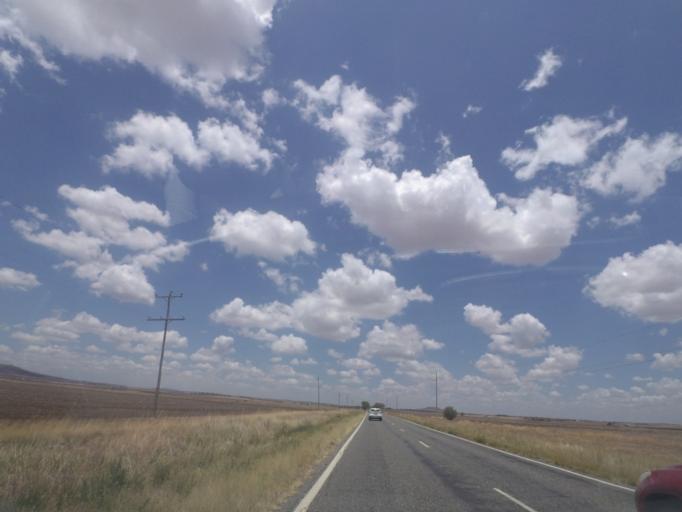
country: AU
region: Queensland
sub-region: Toowoomba
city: Top Camp
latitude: -27.9110
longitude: 151.9796
